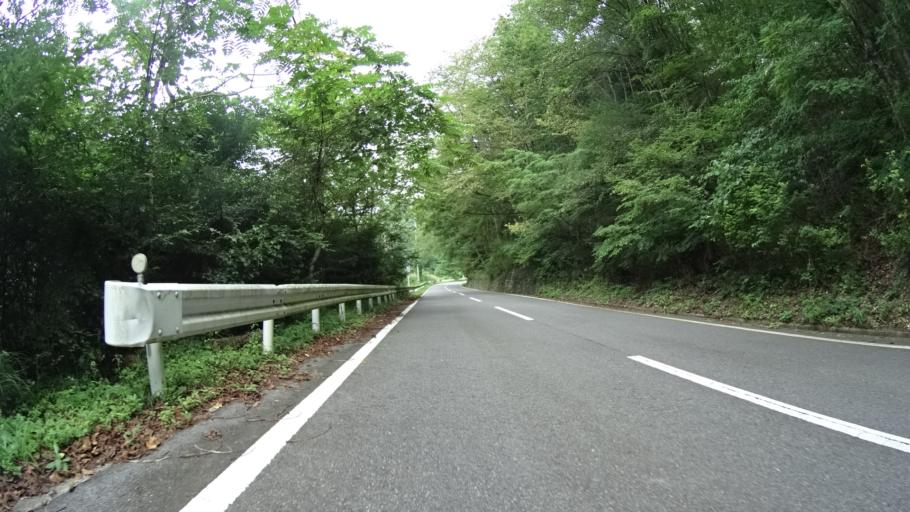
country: JP
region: Yamanashi
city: Kofu-shi
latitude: 35.7641
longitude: 138.5465
